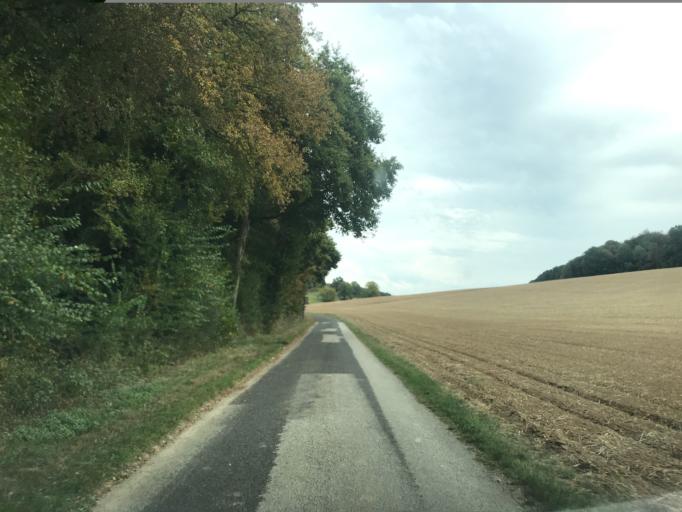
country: FR
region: Haute-Normandie
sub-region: Departement de l'Eure
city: Heudreville-sur-Eure
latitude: 49.0944
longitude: 1.2235
